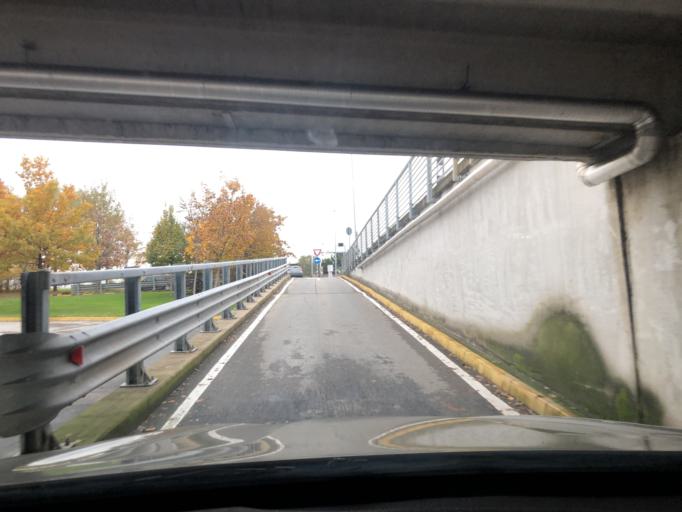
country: IT
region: Lombardy
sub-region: Citta metropolitana di Milano
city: Carugate
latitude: 45.5472
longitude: 9.3306
